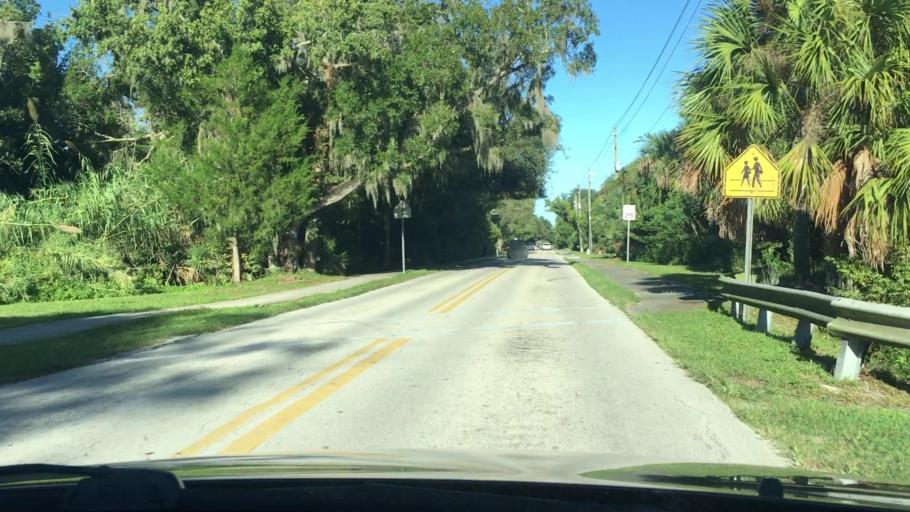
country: US
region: Florida
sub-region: Volusia County
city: Holly Hill
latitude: 29.2488
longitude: -81.0632
